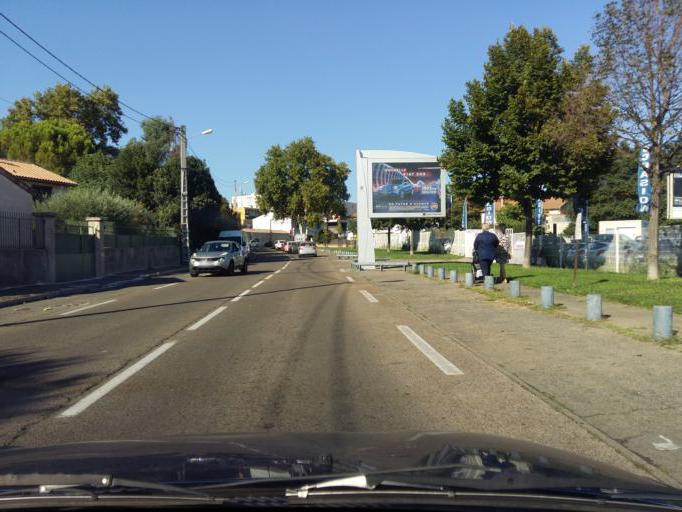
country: FR
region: Languedoc-Roussillon
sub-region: Departement du Gard
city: Nimes
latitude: 43.8202
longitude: 4.3467
